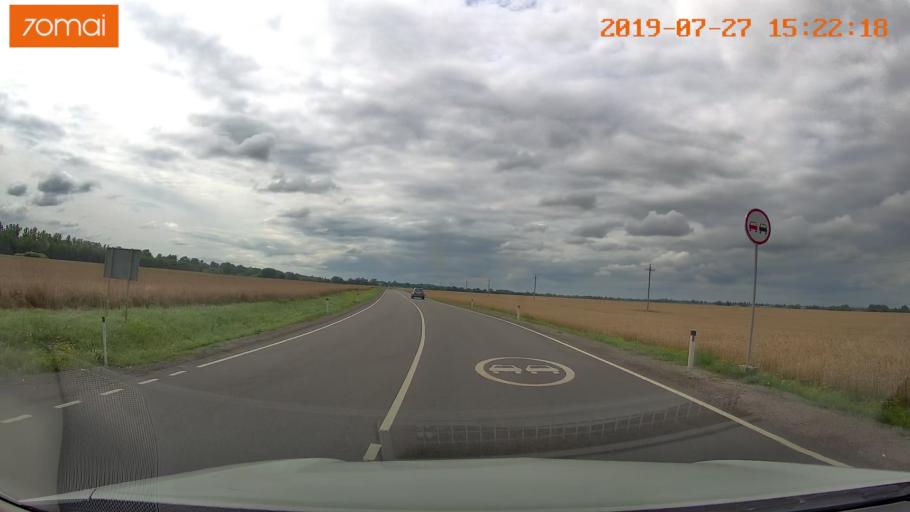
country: RU
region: Kaliningrad
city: Nesterov
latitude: 54.6338
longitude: 22.6627
